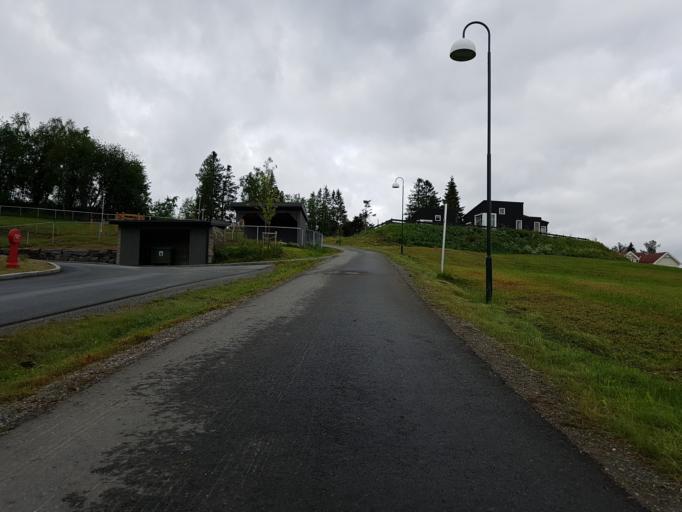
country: NO
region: Sor-Trondelag
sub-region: Selbu
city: Mebonden
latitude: 63.2212
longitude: 11.0315
